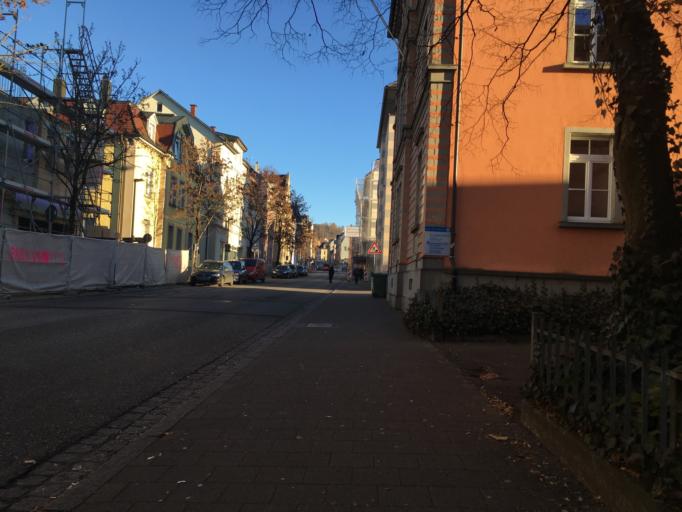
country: DE
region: Baden-Wuerttemberg
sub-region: Tuebingen Region
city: Ravensburg
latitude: 47.7839
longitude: 9.6075
